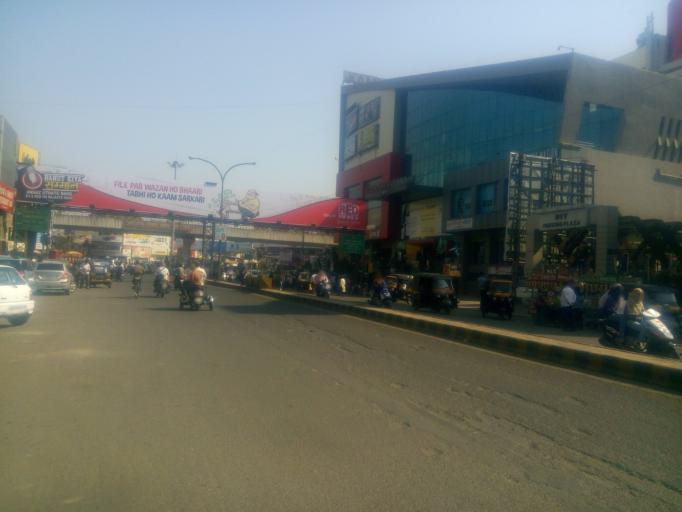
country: IN
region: Maharashtra
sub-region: Nagpur Division
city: Nagpur
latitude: 21.1438
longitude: 79.0797
